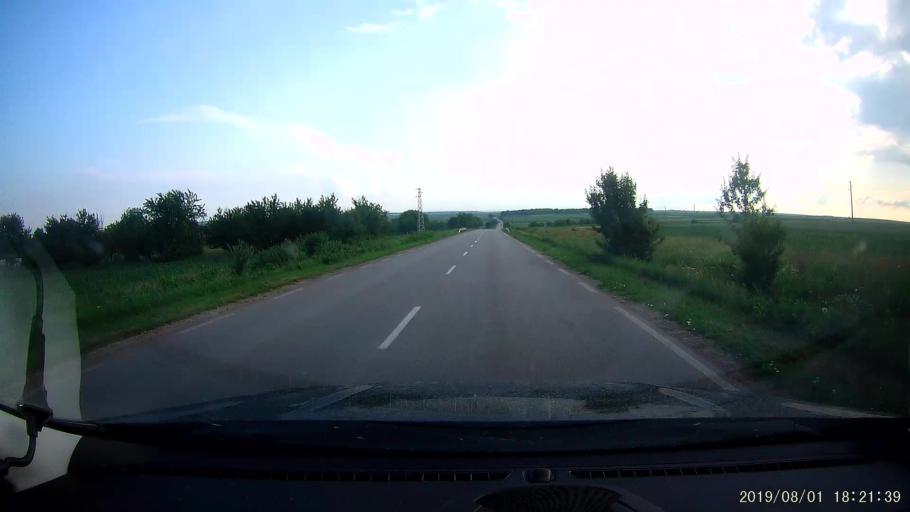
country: BG
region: Shumen
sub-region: Obshtina Kaolinovo
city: Kaolinovo
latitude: 43.6502
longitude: 27.0685
